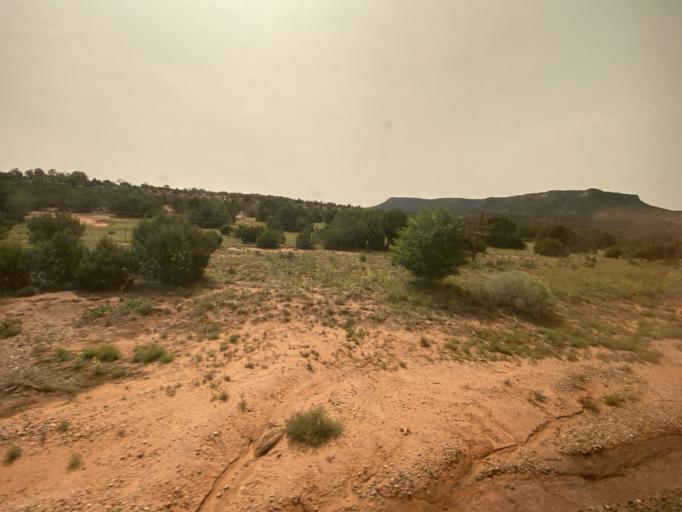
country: US
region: New Mexico
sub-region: San Miguel County
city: Pecos
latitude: 35.3913
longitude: -105.4804
